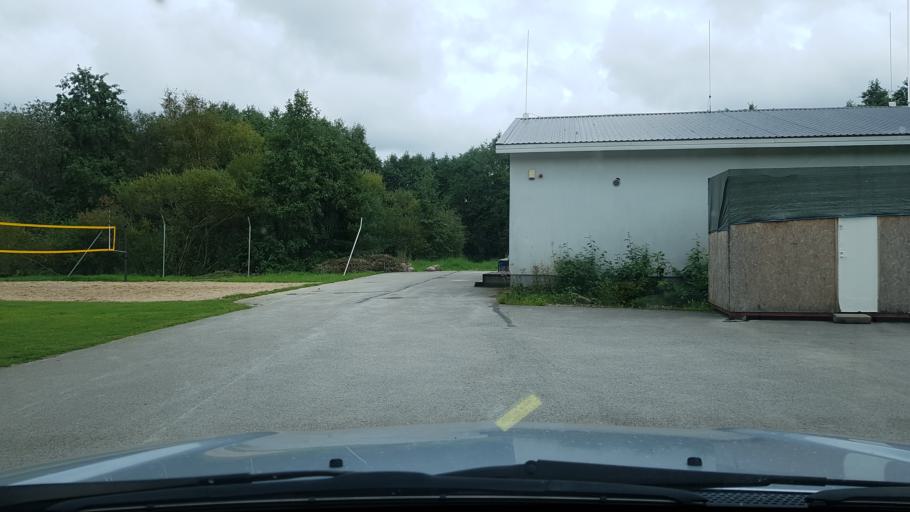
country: EE
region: Harju
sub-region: Rae vald
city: Vaida
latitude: 59.3196
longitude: 24.9508
